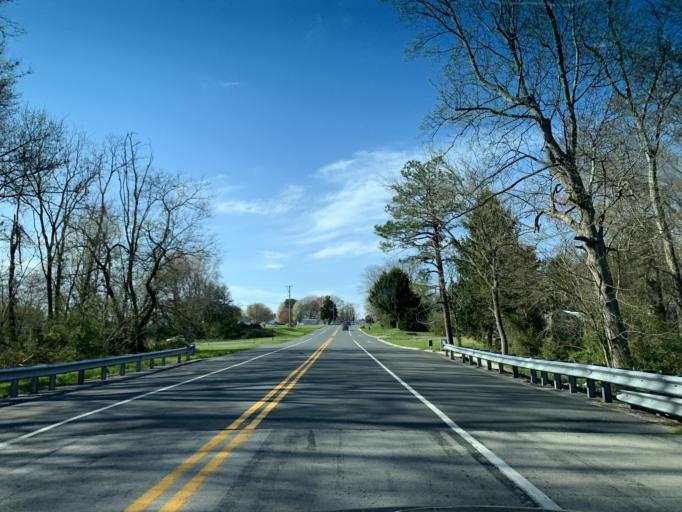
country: US
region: Delaware
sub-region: Kent County
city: Woodside East
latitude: 39.0385
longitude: -75.5529
